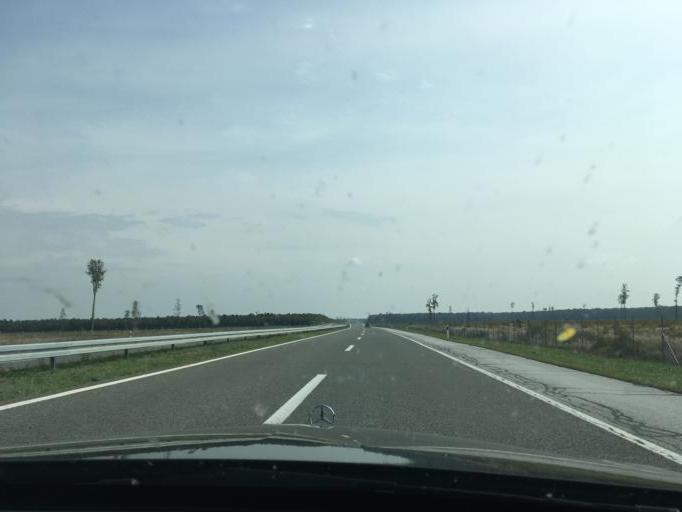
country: HR
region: Vukovarsko-Srijemska
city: Vrbanja
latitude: 45.0458
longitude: 18.8663
